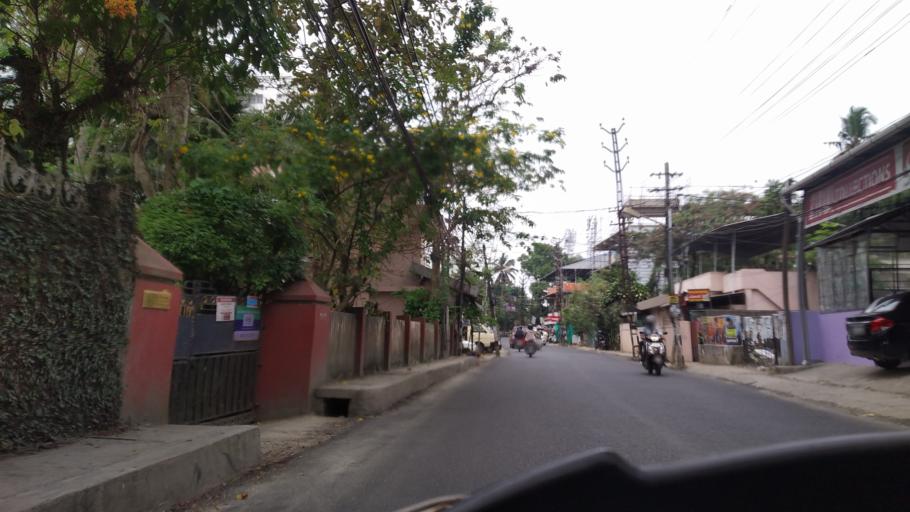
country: IN
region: Kerala
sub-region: Ernakulam
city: Cochin
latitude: 9.9352
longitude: 76.2975
